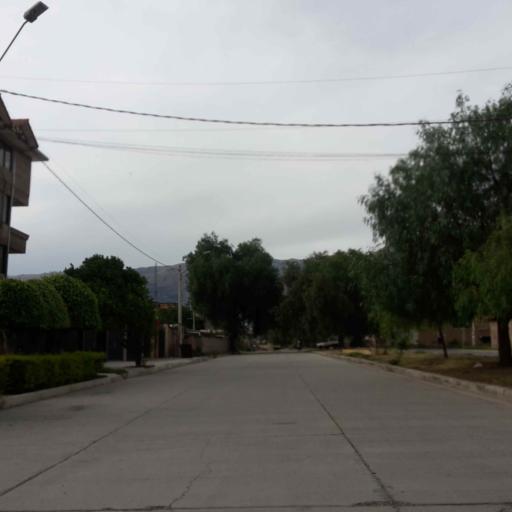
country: BO
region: Cochabamba
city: Cochabamba
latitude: -17.3658
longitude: -66.1893
